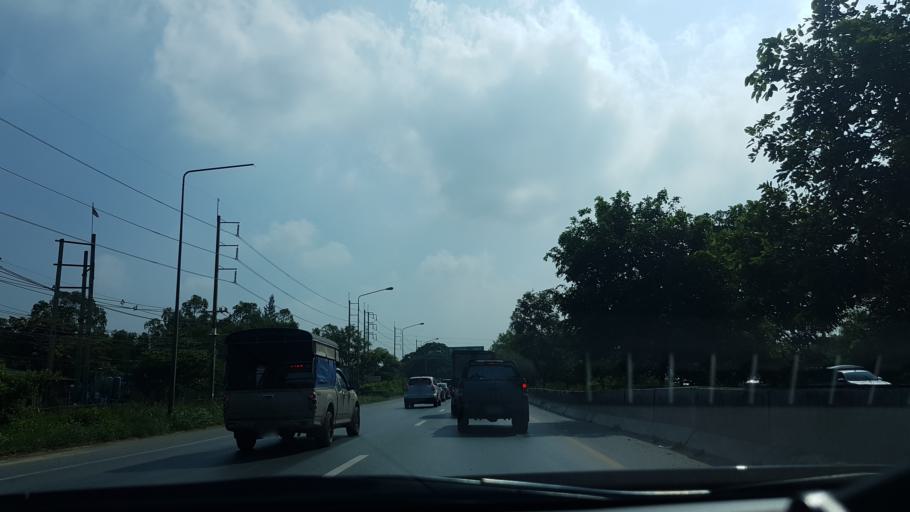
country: TH
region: Phra Nakhon Si Ayutthaya
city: Bang Pa-in
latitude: 14.1696
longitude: 100.6049
